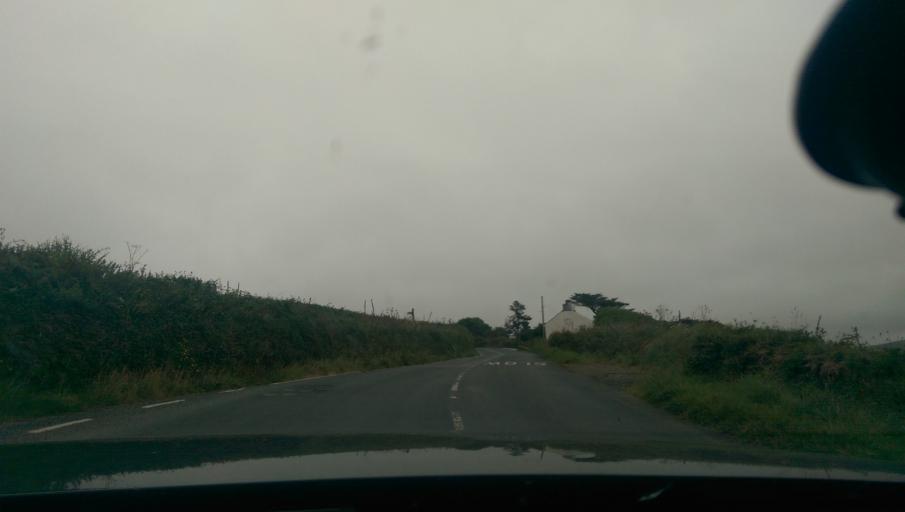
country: GB
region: England
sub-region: Cornwall
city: Saint Just
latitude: 50.1188
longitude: -5.6785
